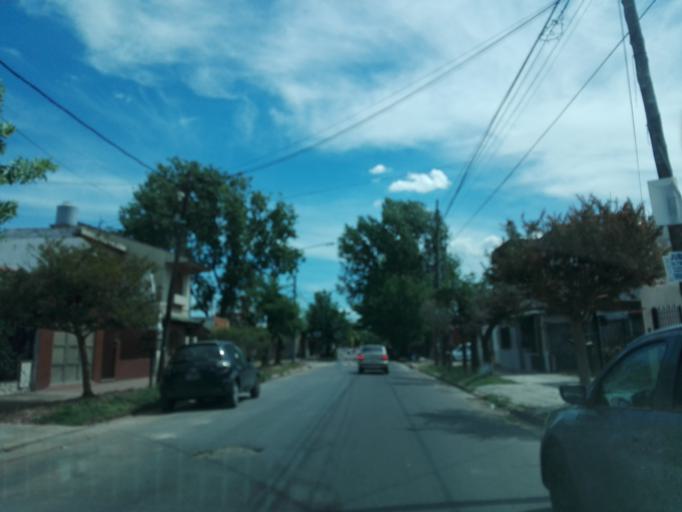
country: AR
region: Buenos Aires
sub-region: Partido de Lanus
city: Lanus
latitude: -34.7214
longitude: -58.3861
